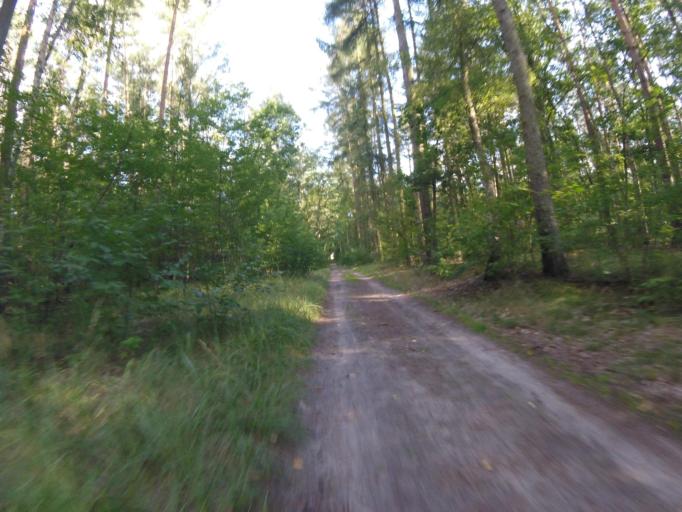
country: DE
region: Brandenburg
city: Schulzendorf
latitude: 52.3261
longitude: 13.5901
